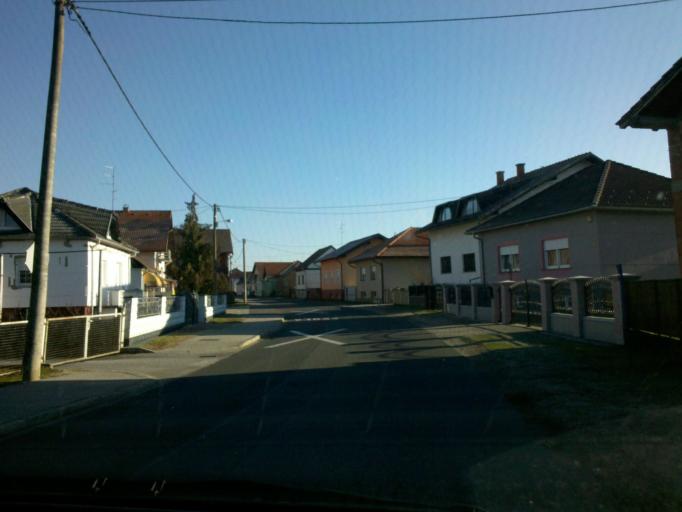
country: HR
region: Medimurska
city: Palovec
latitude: 46.4035
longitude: 16.5620
